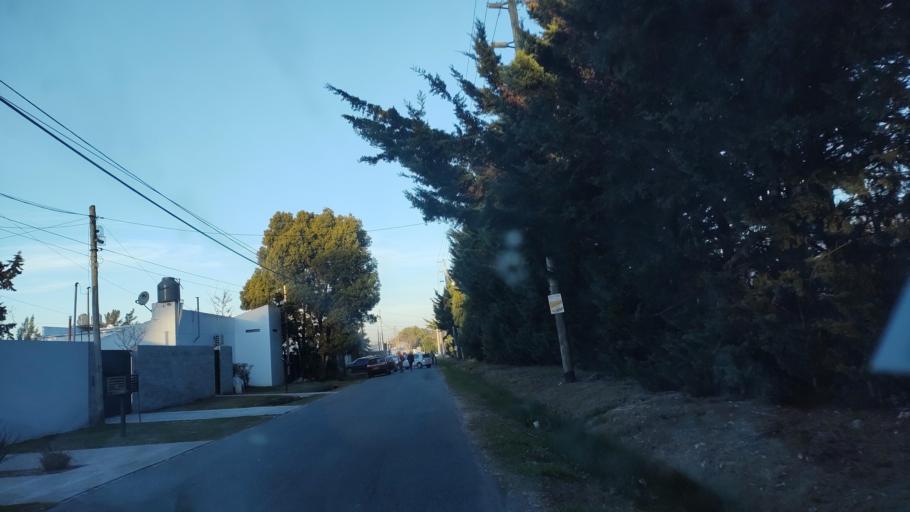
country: AR
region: Buenos Aires
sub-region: Partido de La Plata
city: La Plata
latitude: -34.9051
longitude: -58.0470
